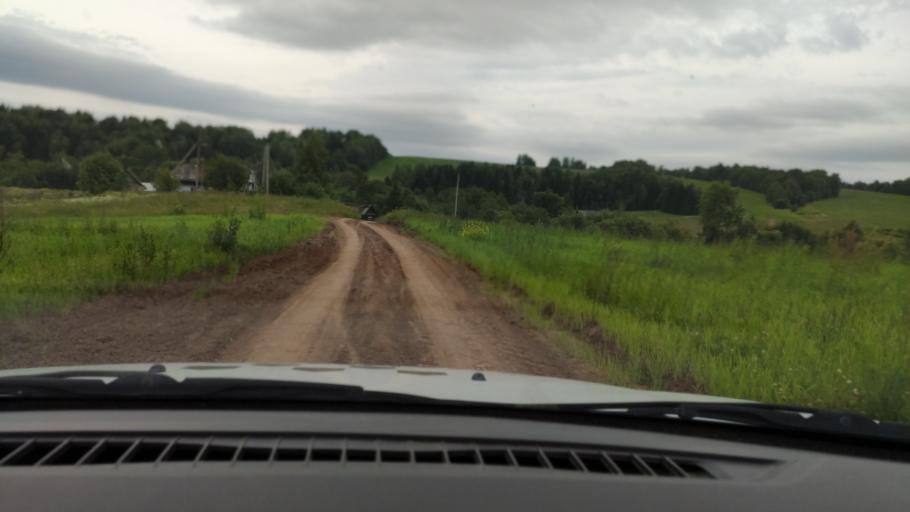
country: RU
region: Perm
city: Orda
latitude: 57.2931
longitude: 56.5940
